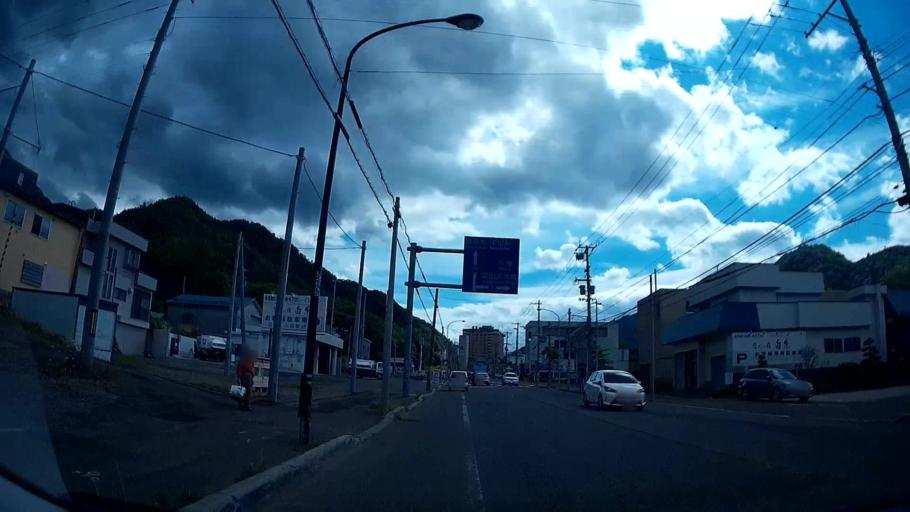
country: JP
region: Hokkaido
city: Sapporo
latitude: 42.9677
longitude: 141.1688
